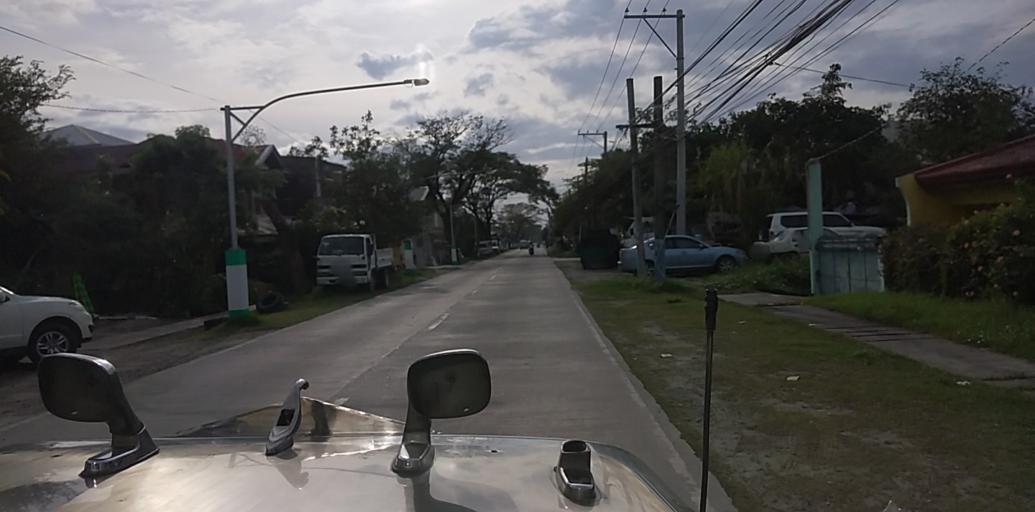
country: PH
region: Central Luzon
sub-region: Province of Pampanga
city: Minalin
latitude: 14.9792
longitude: 120.6915
